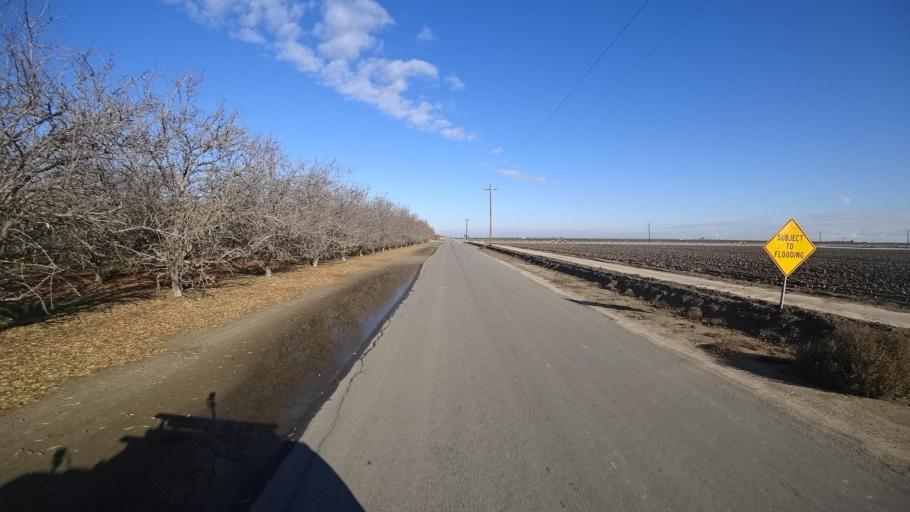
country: US
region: California
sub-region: Kern County
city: McFarland
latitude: 35.7020
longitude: -119.2941
